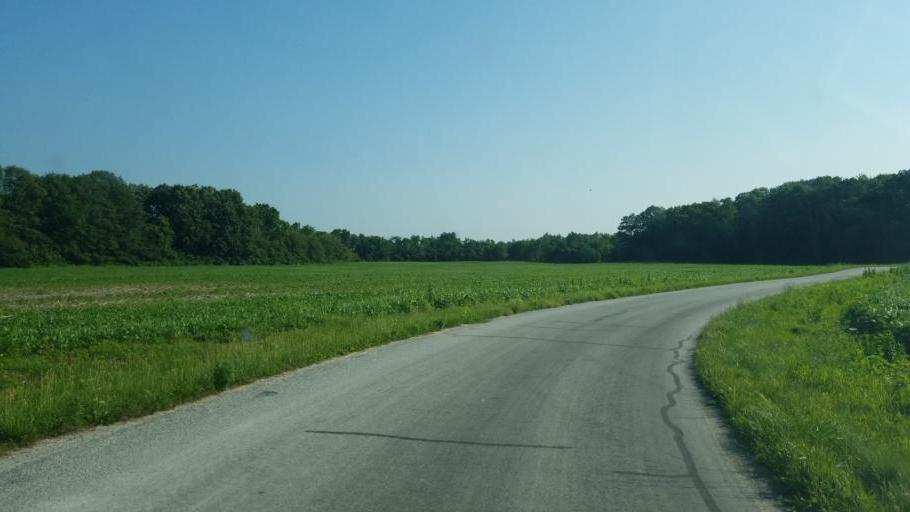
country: US
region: Ohio
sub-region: Hardin County
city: Kenton
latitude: 40.6031
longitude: -83.5426
